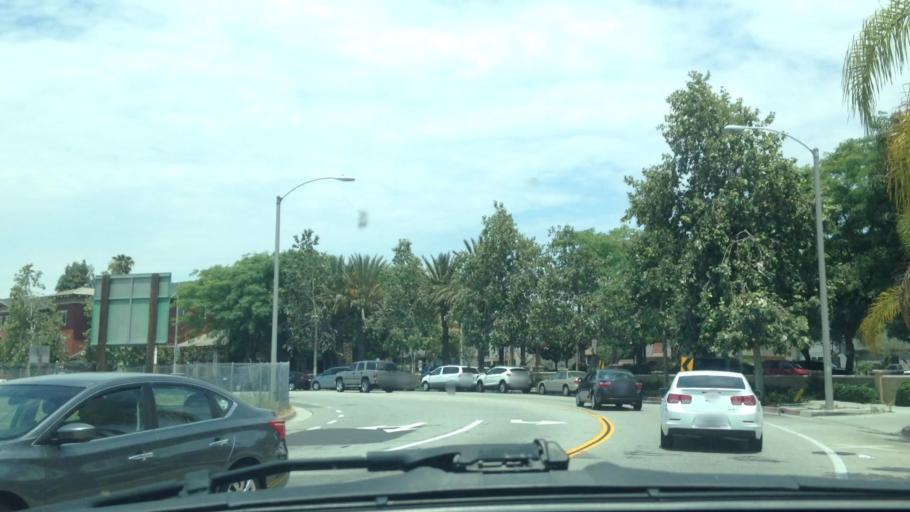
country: US
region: California
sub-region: Orange County
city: Anaheim
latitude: 33.8328
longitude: -117.9302
